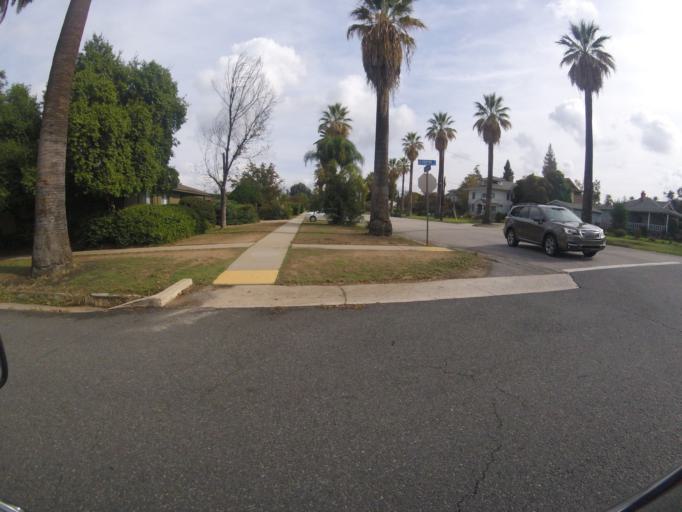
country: US
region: California
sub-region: San Bernardino County
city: Redlands
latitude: 34.0404
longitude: -117.1814
